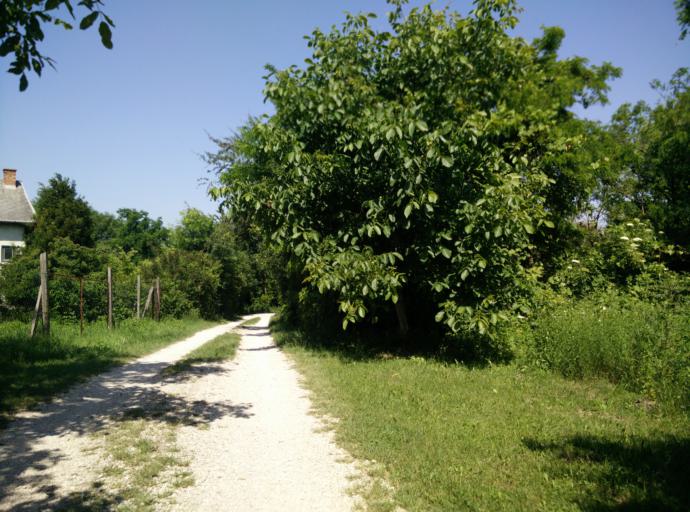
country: HU
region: Pest
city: Biatorbagy
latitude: 47.4712
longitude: 18.8385
